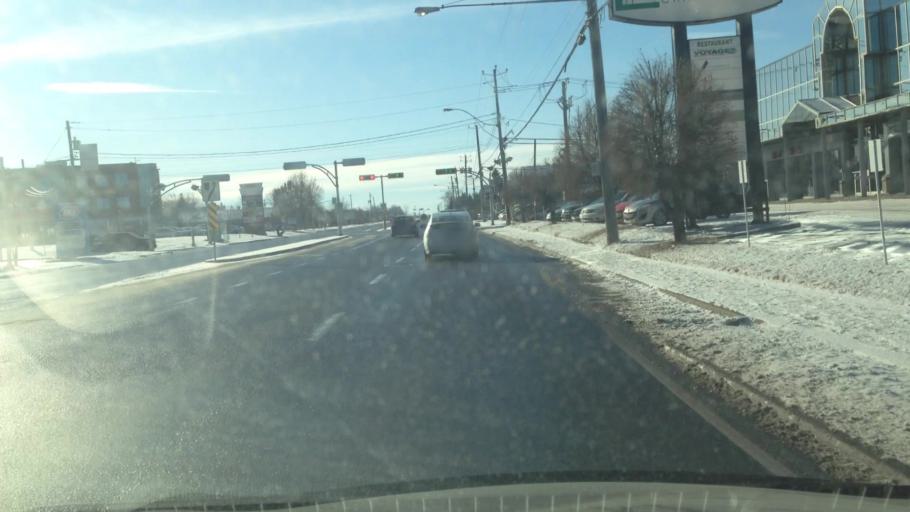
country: CA
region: Quebec
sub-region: Monteregie
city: Chateauguay
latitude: 45.3633
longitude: -73.7133
